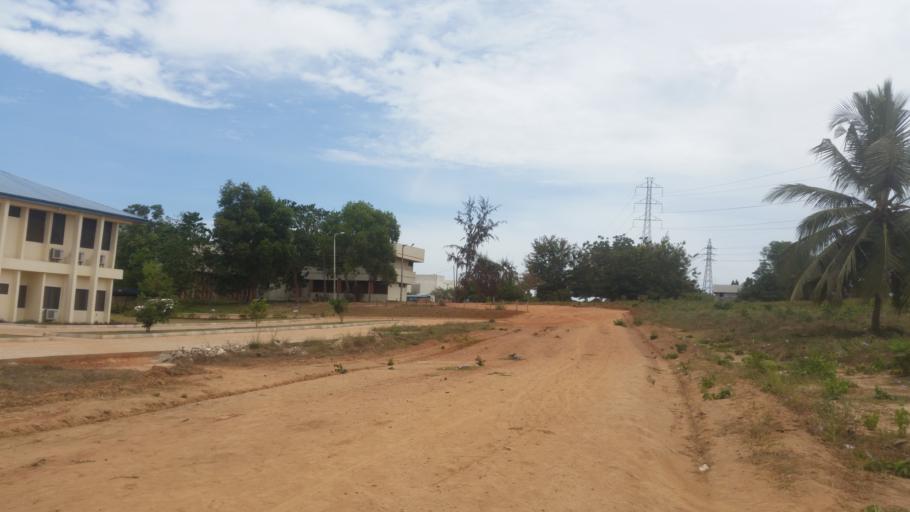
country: GH
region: Central
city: Cape Coast
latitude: 5.1186
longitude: -1.2951
